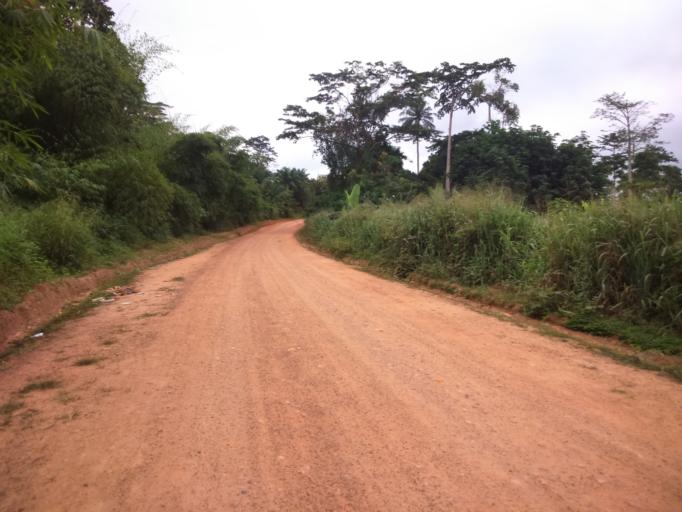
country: CI
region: Lagunes
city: Agou
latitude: 6.0864
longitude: -4.0665
